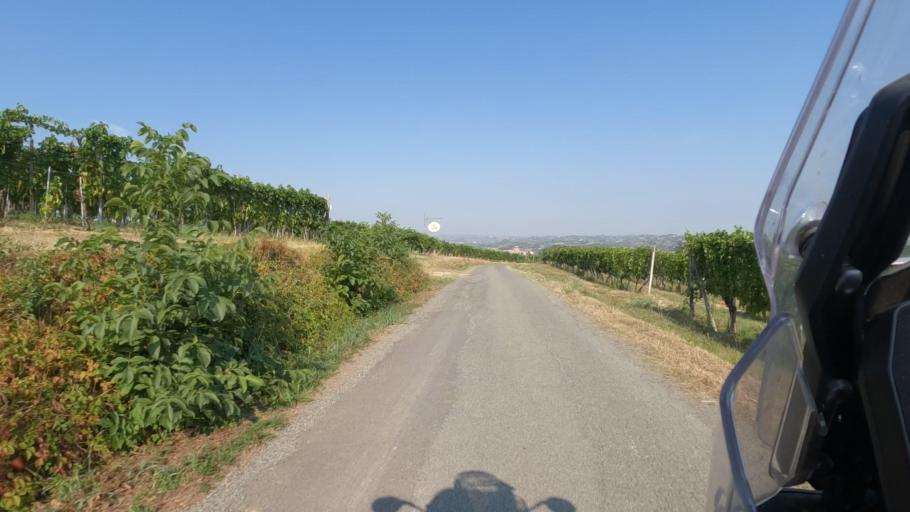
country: IT
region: Piedmont
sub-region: Provincia di Asti
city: Castel Boglione
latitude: 44.7508
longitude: 8.3844
